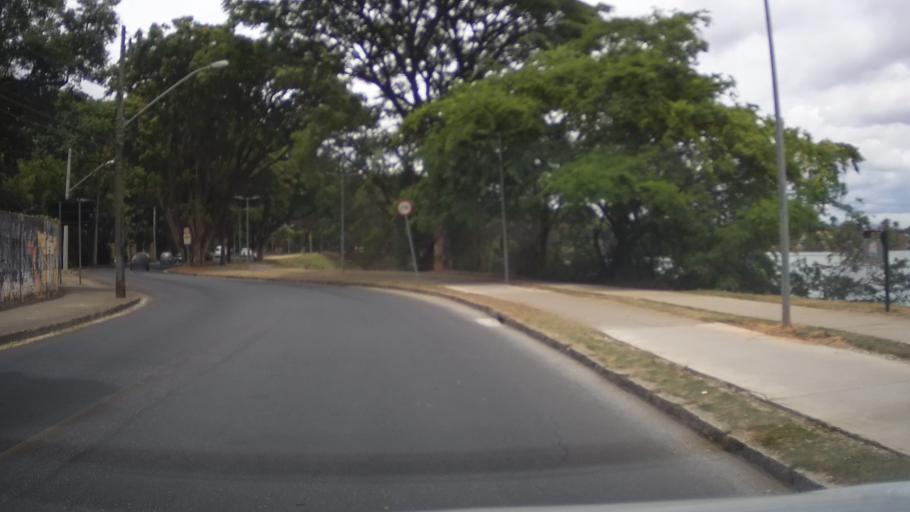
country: BR
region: Minas Gerais
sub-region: Belo Horizonte
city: Belo Horizonte
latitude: -19.8504
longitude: -43.9812
